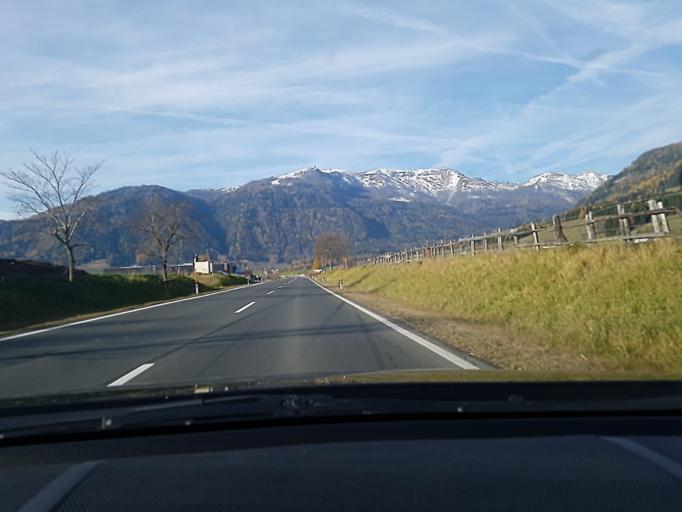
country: AT
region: Salzburg
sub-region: Politischer Bezirk Tamsweg
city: Mauterndorf
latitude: 47.1392
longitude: 13.7054
